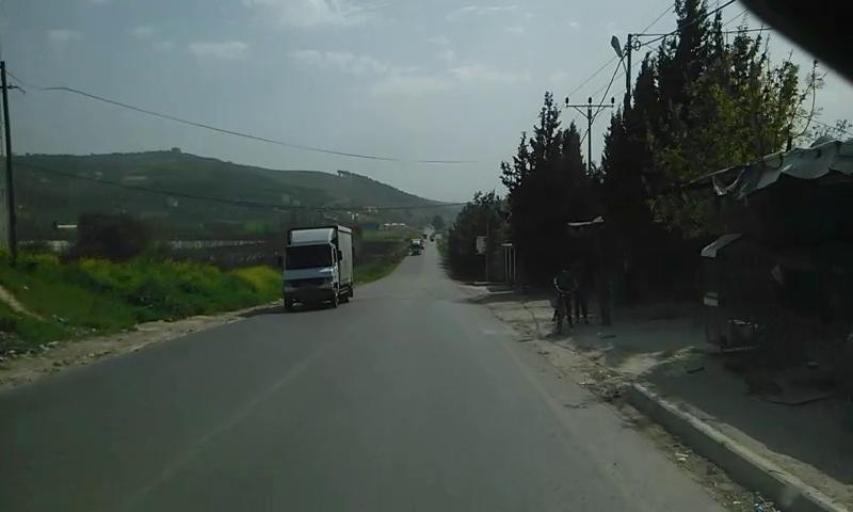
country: PS
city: Bir al Basha
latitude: 32.4157
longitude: 35.2291
